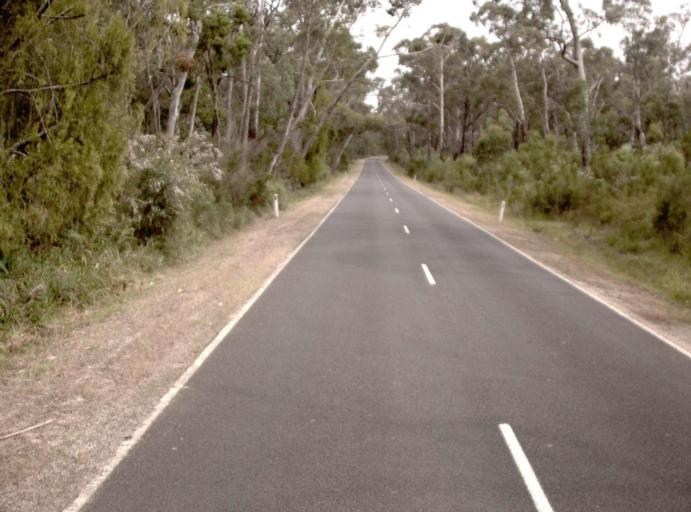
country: AU
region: Victoria
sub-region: Latrobe
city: Traralgon
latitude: -38.4375
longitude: 146.8229
